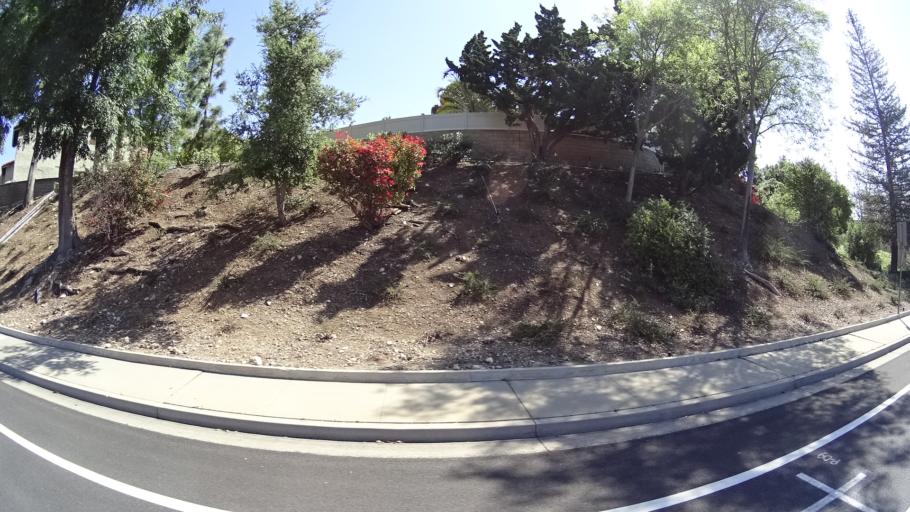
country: US
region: California
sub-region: Ventura County
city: Casa Conejo
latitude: 34.1865
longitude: -118.8927
